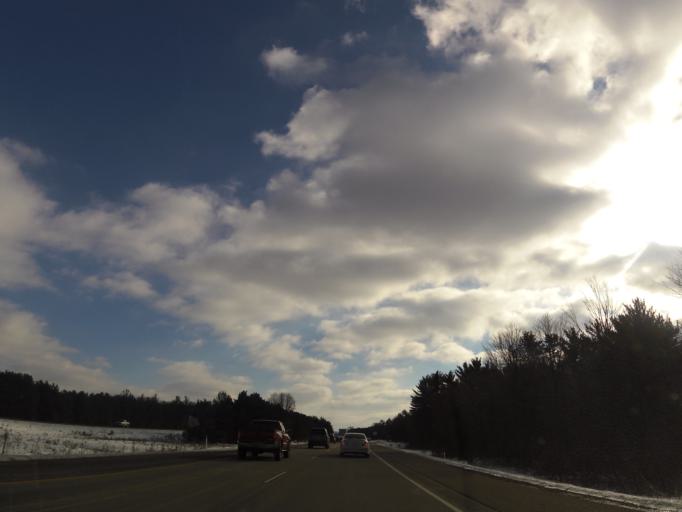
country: US
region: Wisconsin
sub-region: Jackson County
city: Black River Falls
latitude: 44.3791
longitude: -90.9883
